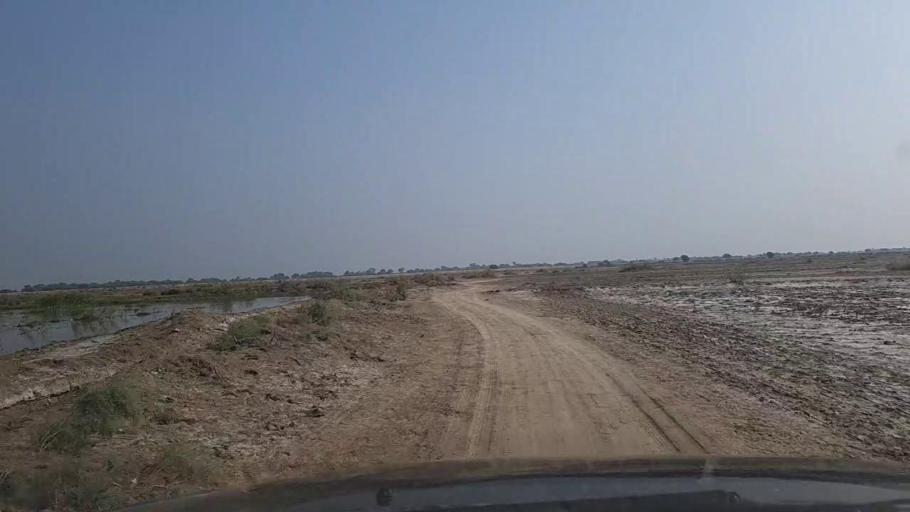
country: PK
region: Sindh
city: Mirpur Batoro
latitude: 24.6766
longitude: 68.2458
